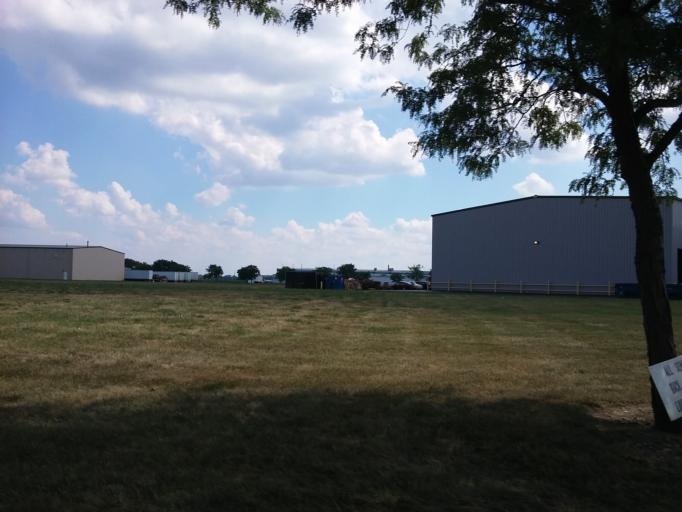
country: US
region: Ohio
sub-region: Wood County
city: Bowling Green
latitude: 41.3819
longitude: -83.6053
